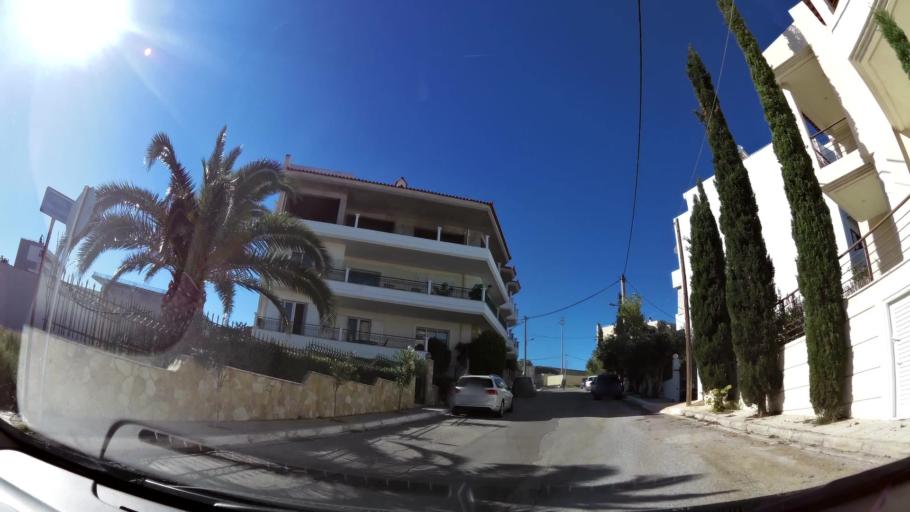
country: GR
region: Attica
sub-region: Nomarchia Anatolikis Attikis
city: Koropi
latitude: 37.9028
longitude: 23.8813
